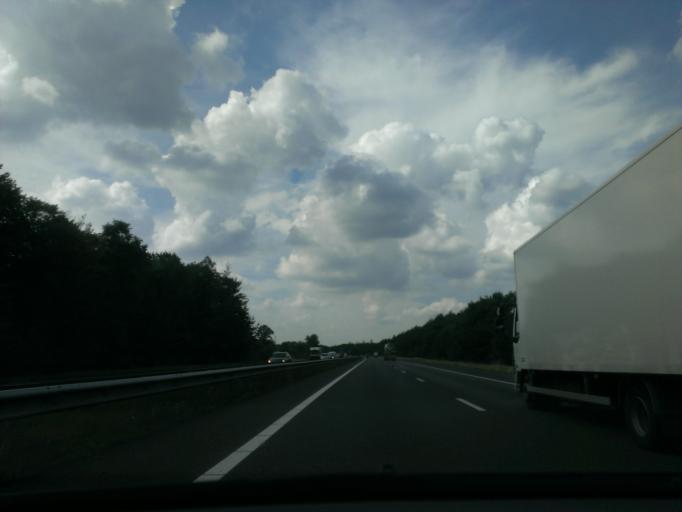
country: NL
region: Gelderland
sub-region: Gemeente Apeldoorn
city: Beekbergen
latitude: 52.1757
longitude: 5.9477
